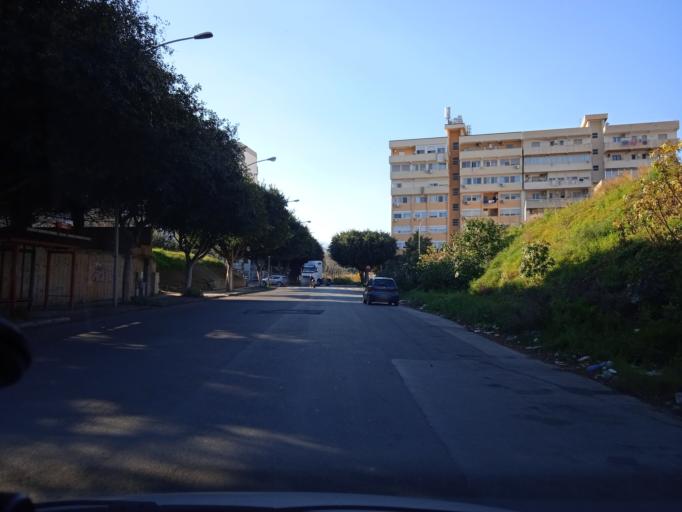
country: IT
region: Sicily
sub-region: Palermo
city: Ciaculli
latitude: 38.1074
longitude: 13.3785
